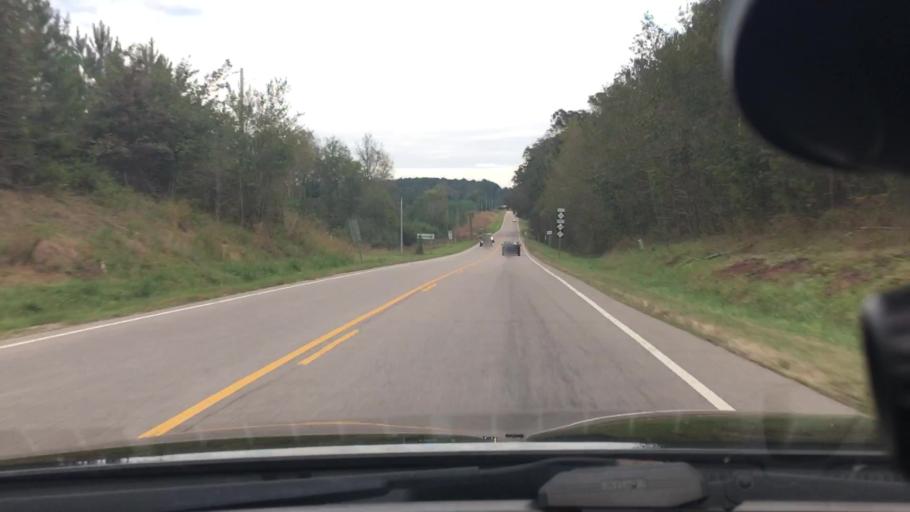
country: US
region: North Carolina
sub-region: Moore County
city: Carthage
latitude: 35.3837
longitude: -79.4873
